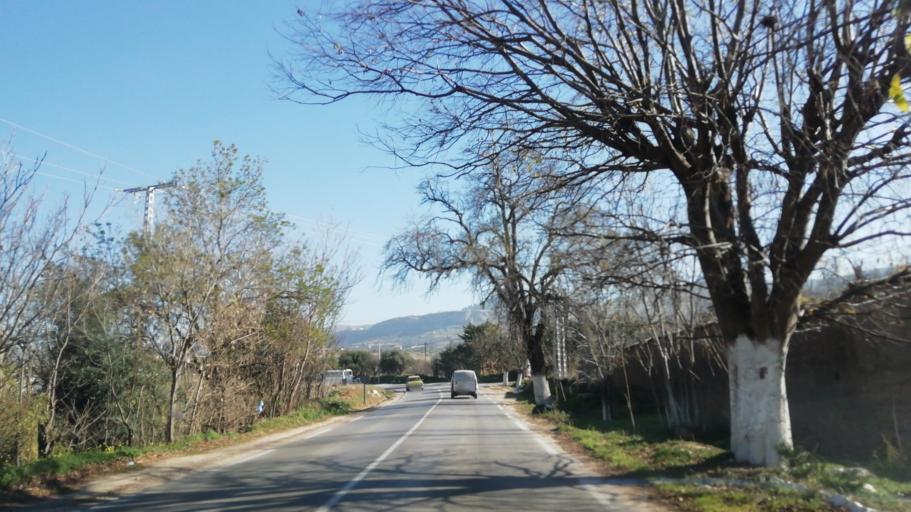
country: DZ
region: Tlemcen
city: Mansoura
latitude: 34.8635
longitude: -1.3597
